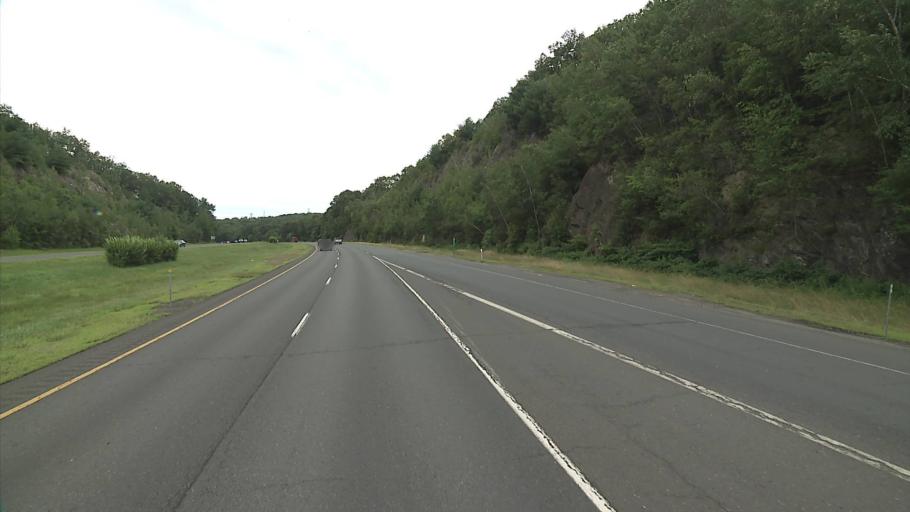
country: US
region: Connecticut
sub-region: Litchfield County
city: Oakville
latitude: 41.6017
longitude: -73.0666
